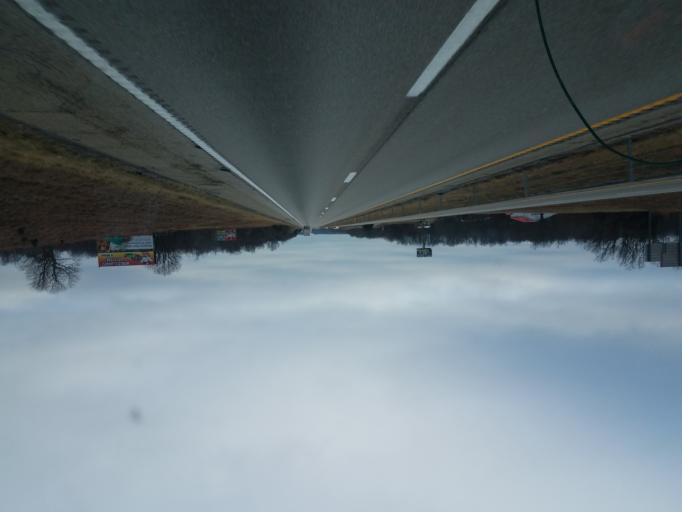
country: US
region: Missouri
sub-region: Laclede County
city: Lebanon
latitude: 37.5902
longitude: -92.7328
